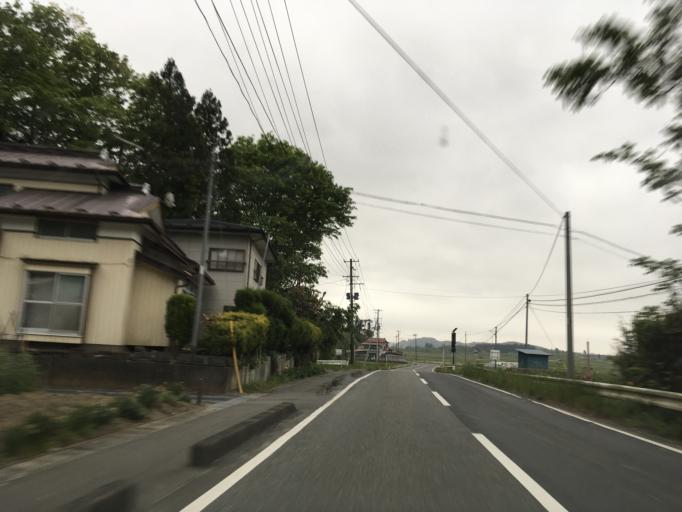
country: JP
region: Miyagi
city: Wakuya
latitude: 38.7292
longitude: 141.2980
